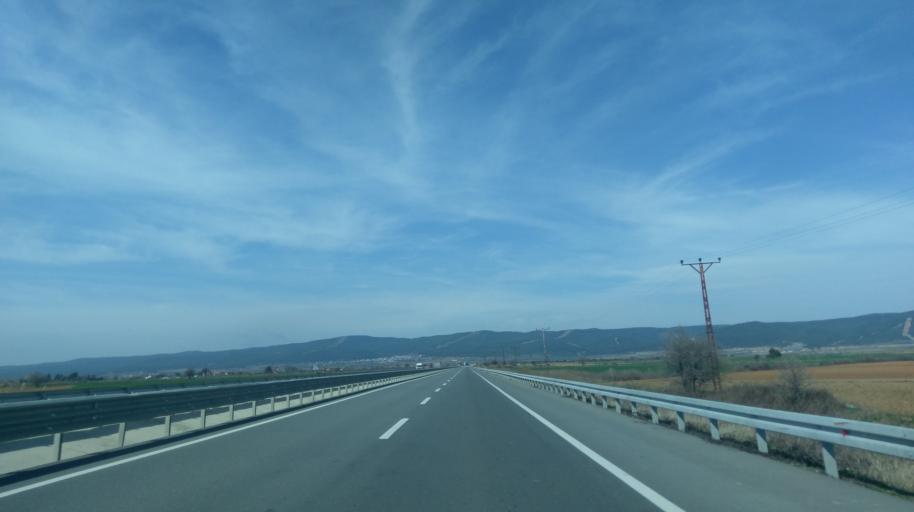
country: TR
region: Canakkale
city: Evrese
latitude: 40.6589
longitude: 26.8171
